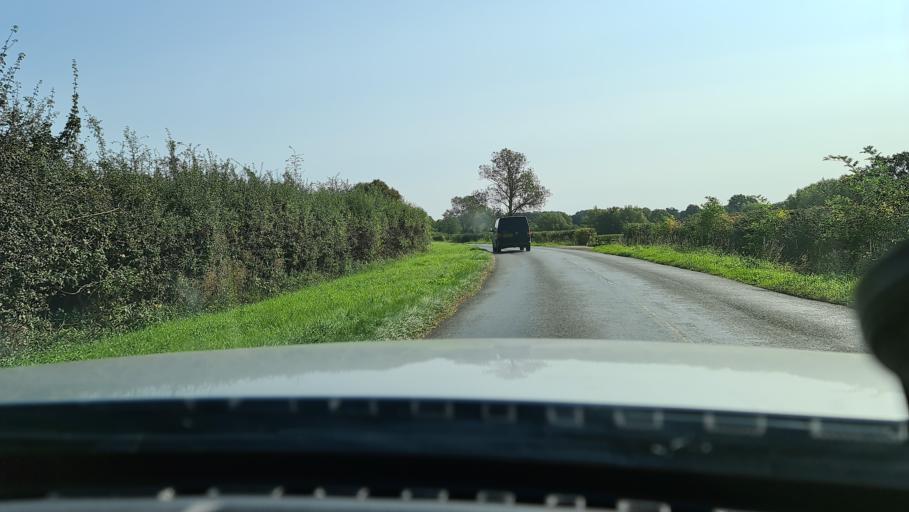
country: GB
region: England
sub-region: Oxfordshire
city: Adderbury
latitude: 52.0297
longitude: -1.2864
